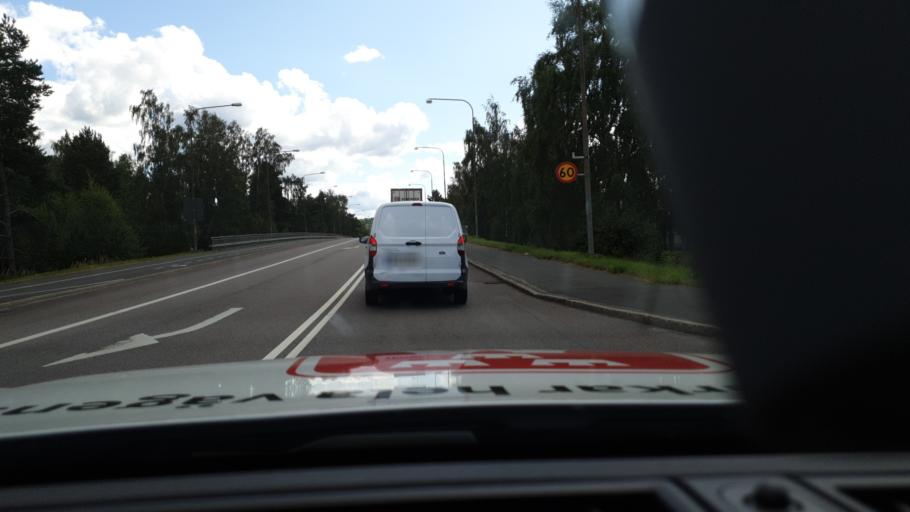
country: SE
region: Joenkoeping
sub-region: Jonkopings Kommun
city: Jonkoping
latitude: 57.7607
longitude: 14.1678
